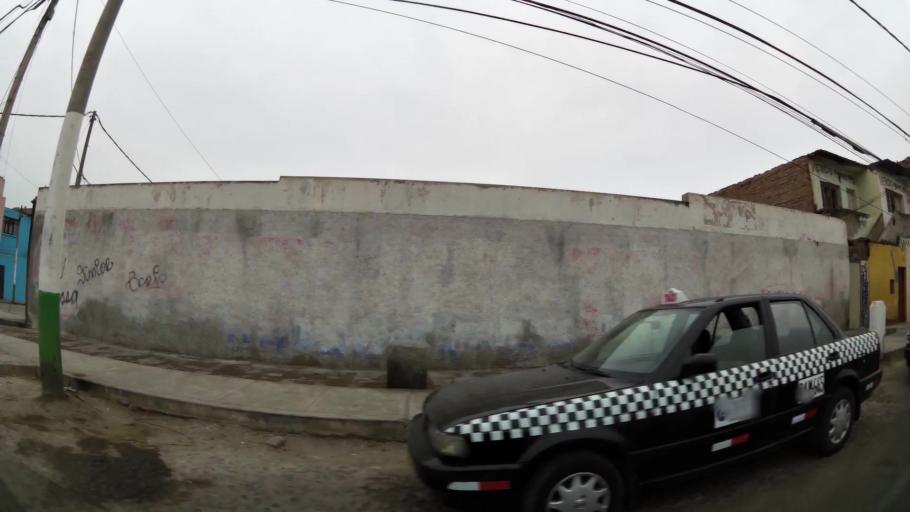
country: PE
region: Callao
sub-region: Callao
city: Callao
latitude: -12.0707
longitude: -77.1280
